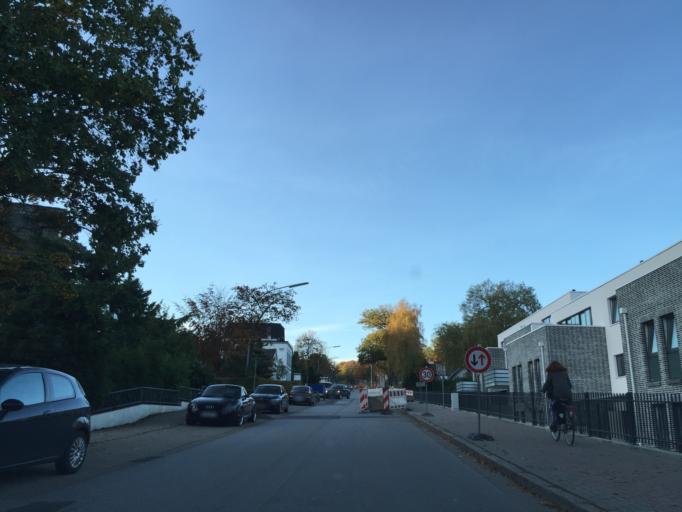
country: DK
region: South Denmark
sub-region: Aabenraa Kommune
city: Krusa
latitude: 54.8294
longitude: 9.4169
